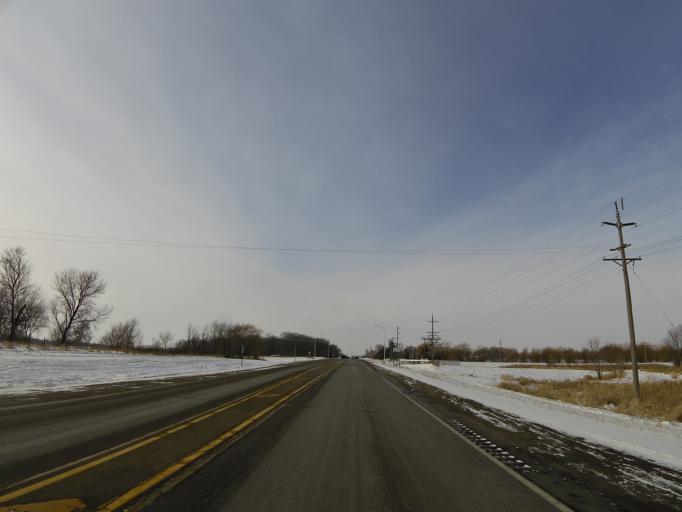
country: US
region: Minnesota
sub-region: McLeod County
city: Lester Prairie
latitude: 44.9063
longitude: -94.0498
